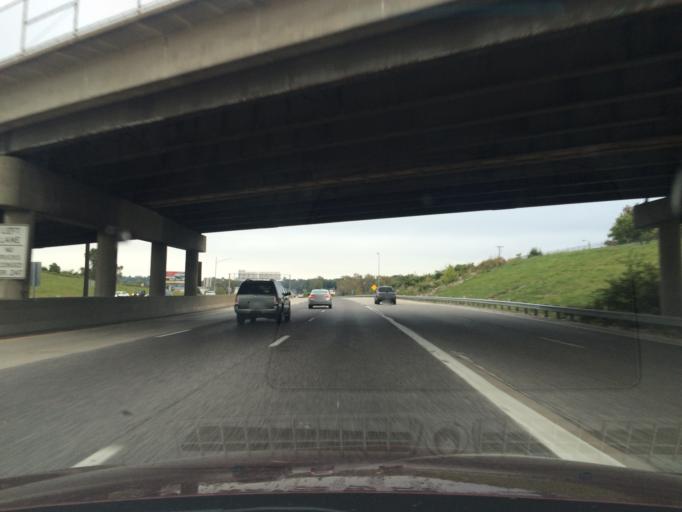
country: US
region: Missouri
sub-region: Saint Louis County
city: Bridgeton
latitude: 38.7467
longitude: -90.4348
